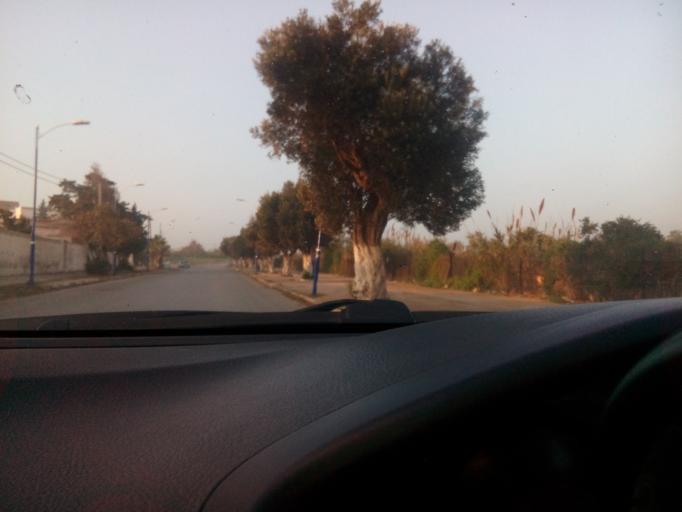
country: DZ
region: Oran
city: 'Ain el Turk
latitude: 35.7415
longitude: -0.7748
